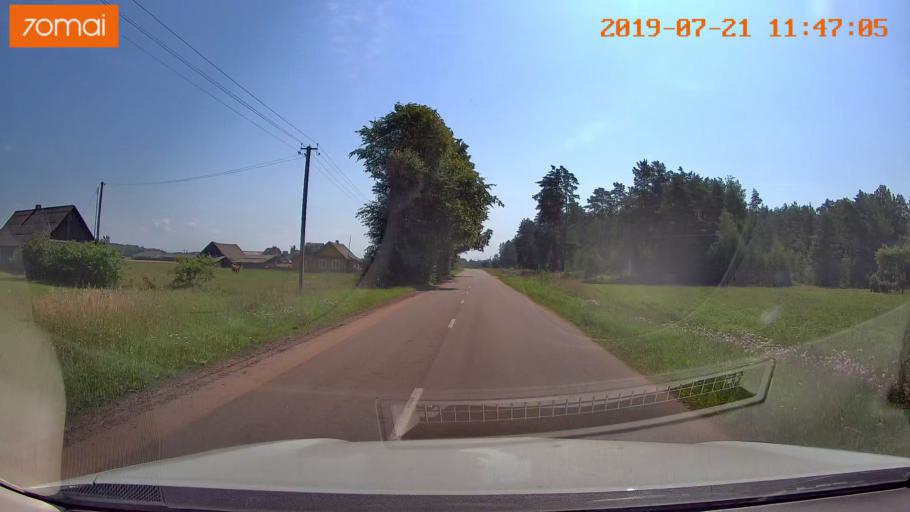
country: BY
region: Grodnenskaya
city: Lyubcha
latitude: 53.9044
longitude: 26.0411
